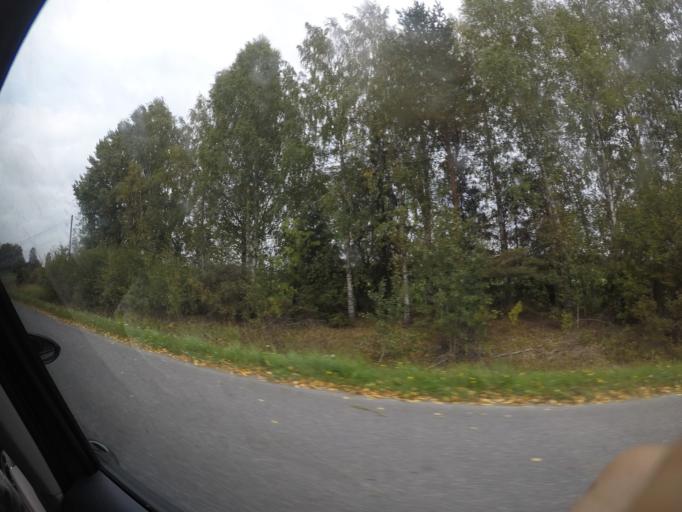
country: FI
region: Haeme
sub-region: Haemeenlinna
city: Haemeenlinna
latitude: 61.0307
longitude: 24.4177
